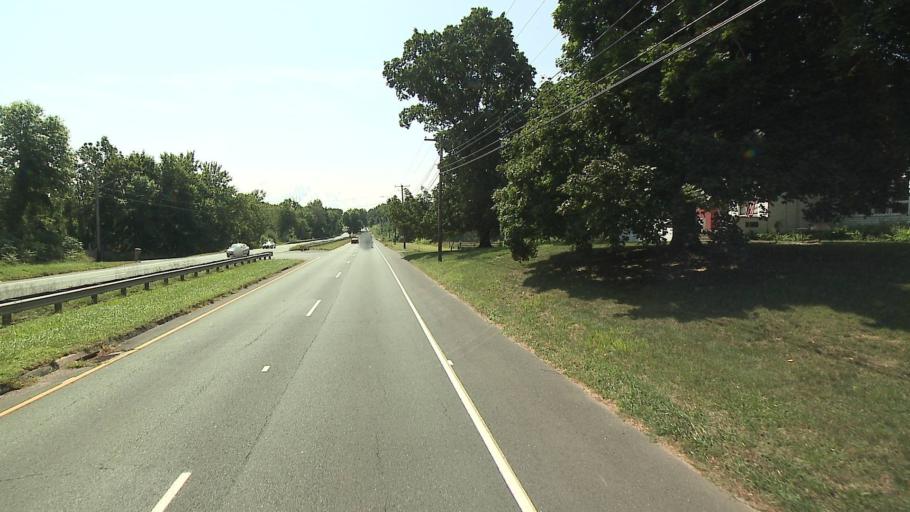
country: US
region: Connecticut
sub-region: Hartford County
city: Windsor
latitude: 41.8646
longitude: -72.6045
